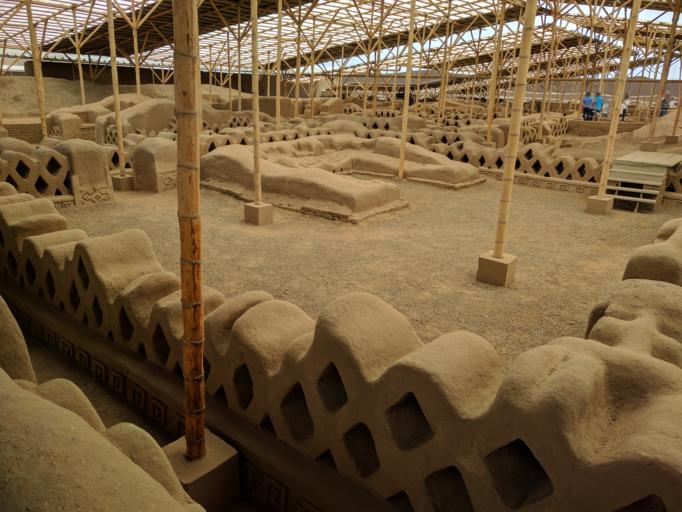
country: PE
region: La Libertad
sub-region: Provincia de Trujillo
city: Buenos Aires
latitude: -8.1100
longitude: -79.0751
